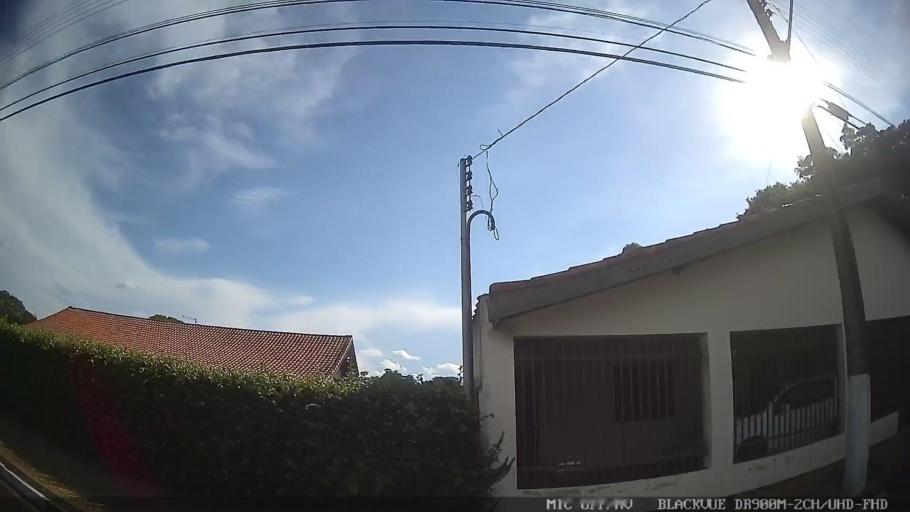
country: BR
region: Sao Paulo
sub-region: Laranjal Paulista
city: Laranjal Paulista
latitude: -23.0851
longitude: -47.7859
